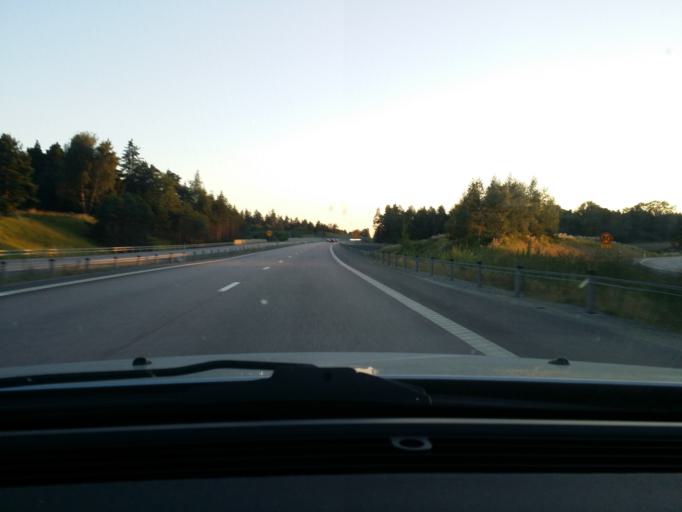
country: SE
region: Uppsala
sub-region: Enkopings Kommun
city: Enkoping
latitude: 59.6472
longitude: 17.0580
